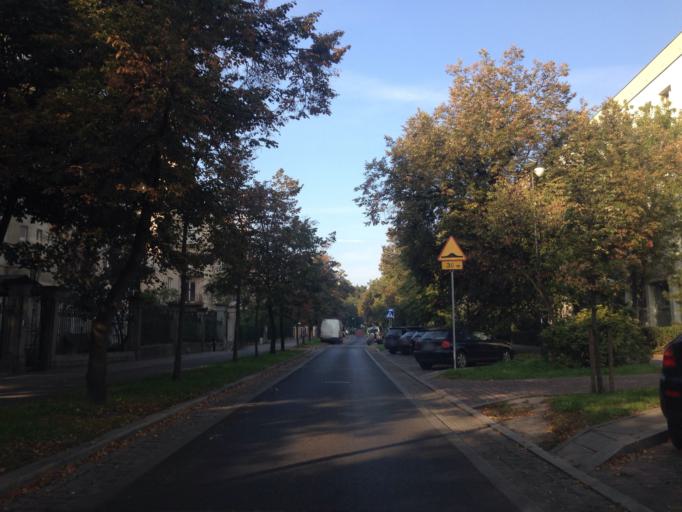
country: PL
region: Kujawsko-Pomorskie
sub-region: Torun
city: Torun
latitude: 53.0119
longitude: 18.5960
